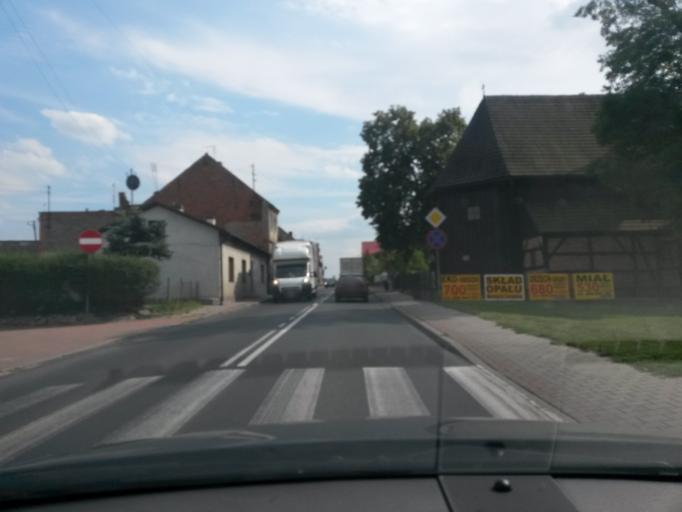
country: PL
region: Greater Poland Voivodeship
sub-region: Powiat sremski
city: Dolsk
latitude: 51.9880
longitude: 17.0661
